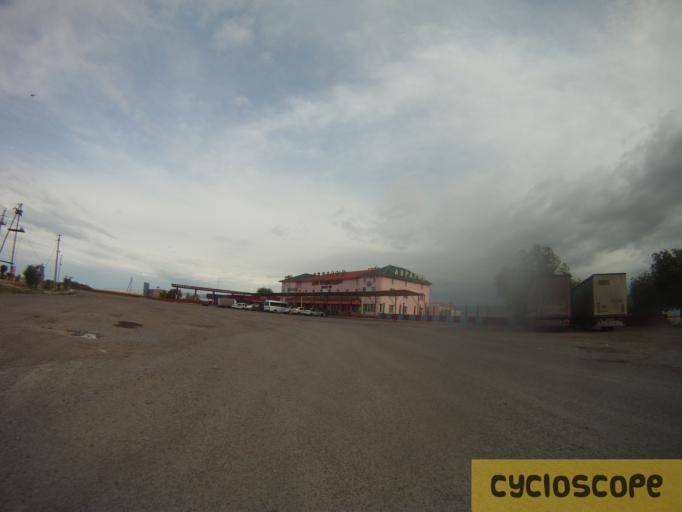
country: KG
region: Chuy
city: Ivanovka
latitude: 43.3799
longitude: 75.2138
